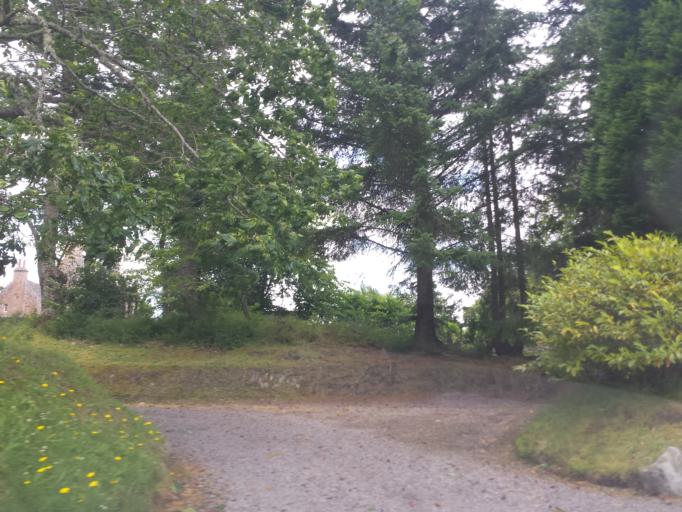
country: GB
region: Scotland
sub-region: Highland
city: Fortrose
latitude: 57.5087
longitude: -4.0418
